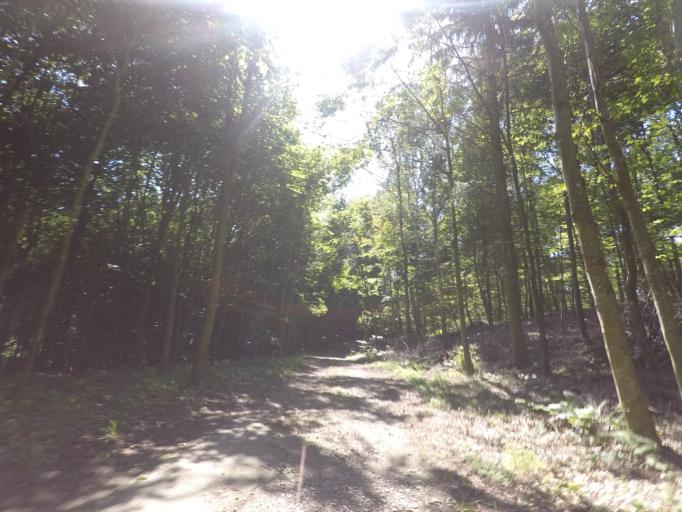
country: LU
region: Luxembourg
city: Bridel
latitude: 49.6434
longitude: 6.0772
